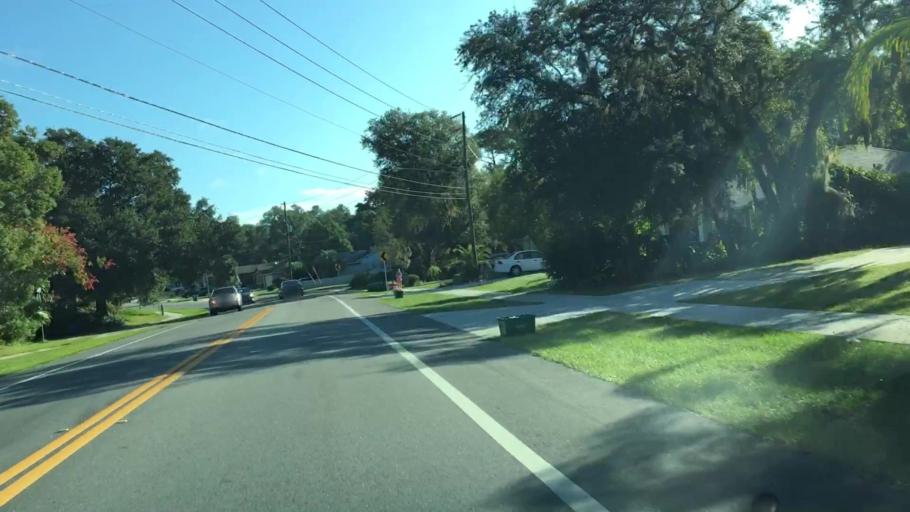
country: US
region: Florida
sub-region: Volusia County
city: Deltona
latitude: 28.8702
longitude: -81.2453
